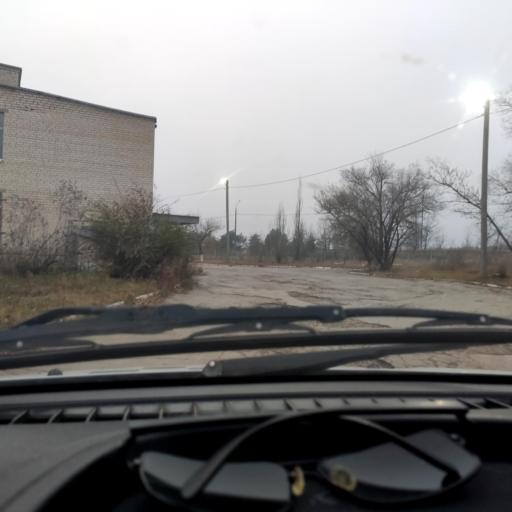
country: RU
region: Samara
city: Zhigulevsk
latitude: 53.4918
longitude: 49.5298
